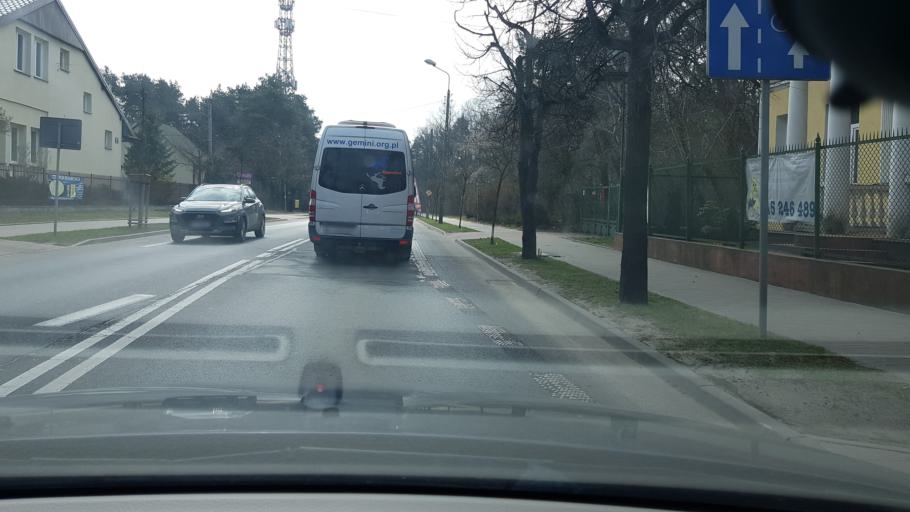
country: PL
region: Masovian Voivodeship
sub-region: Warszawa
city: Wesola
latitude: 52.2503
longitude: 21.2237
